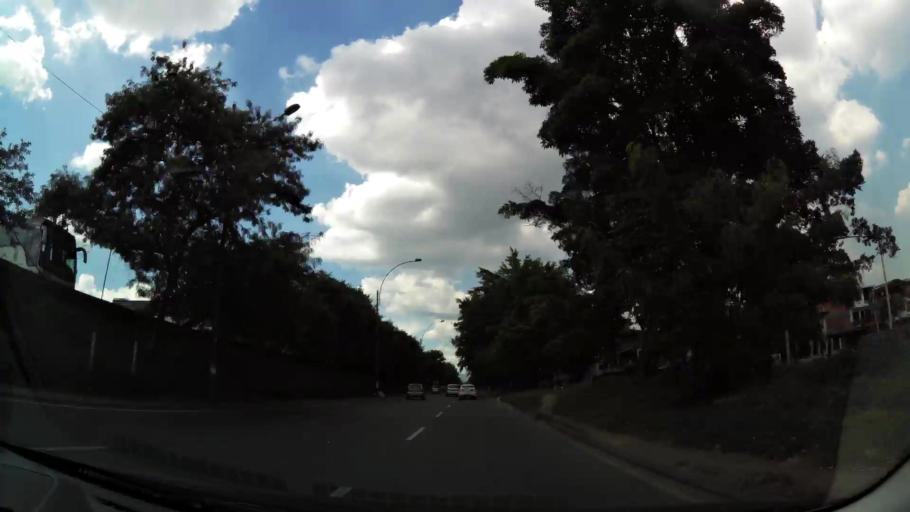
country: CO
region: Valle del Cauca
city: Cali
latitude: 3.4122
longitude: -76.5214
